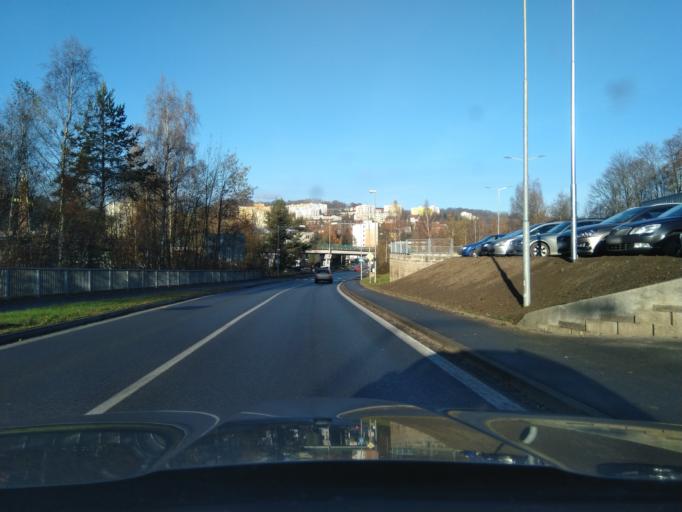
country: CZ
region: Jihocesky
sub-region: Okres Prachatice
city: Vimperk
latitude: 49.0566
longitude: 13.7876
